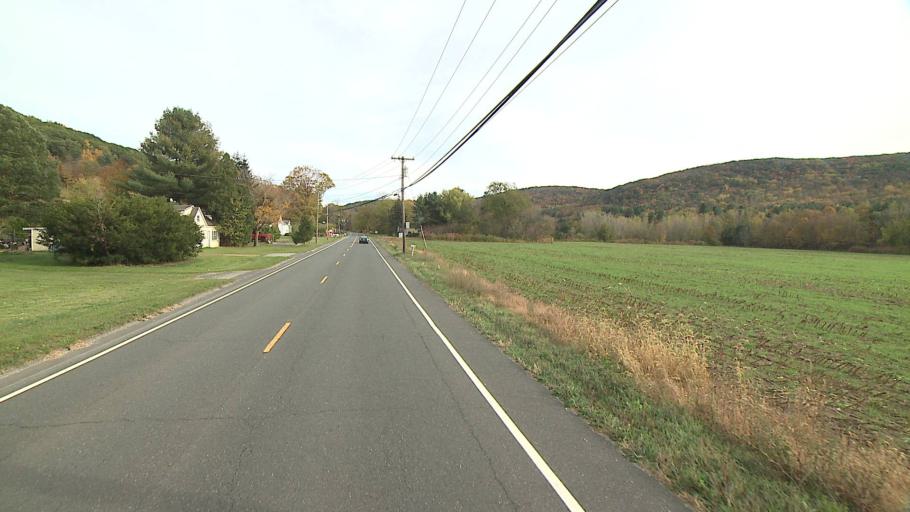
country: US
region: Connecticut
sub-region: Litchfield County
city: Canaan
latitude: 42.0087
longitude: -73.2598
